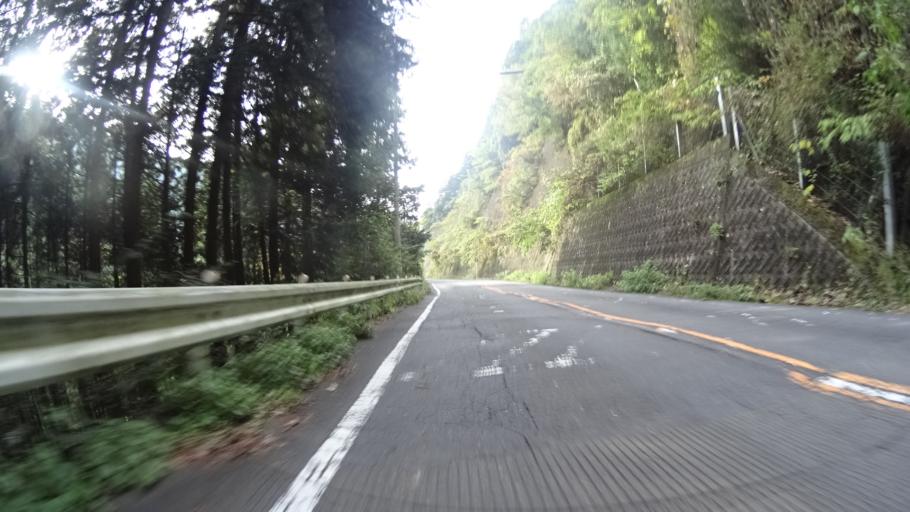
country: JP
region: Yamanashi
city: Uenohara
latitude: 35.6855
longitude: 139.0997
